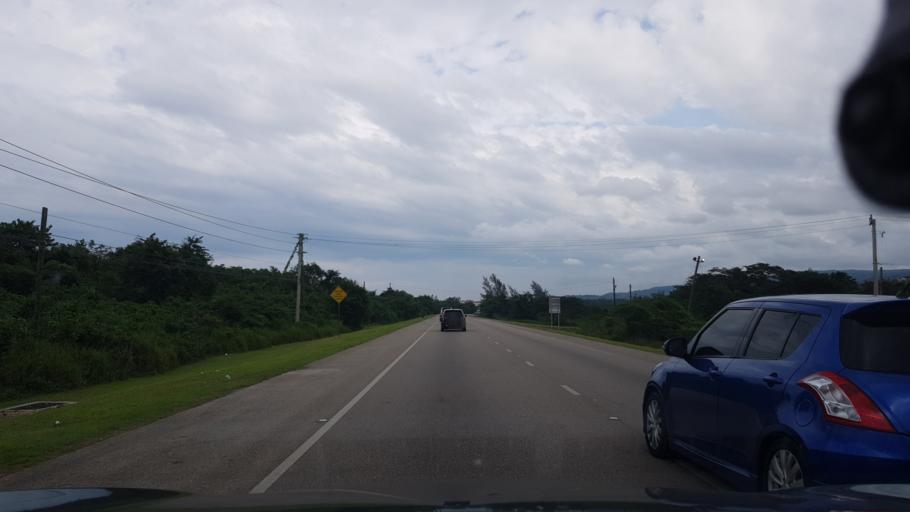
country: JM
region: Saint Ann
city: Runaway Bay
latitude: 18.4614
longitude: -77.3670
